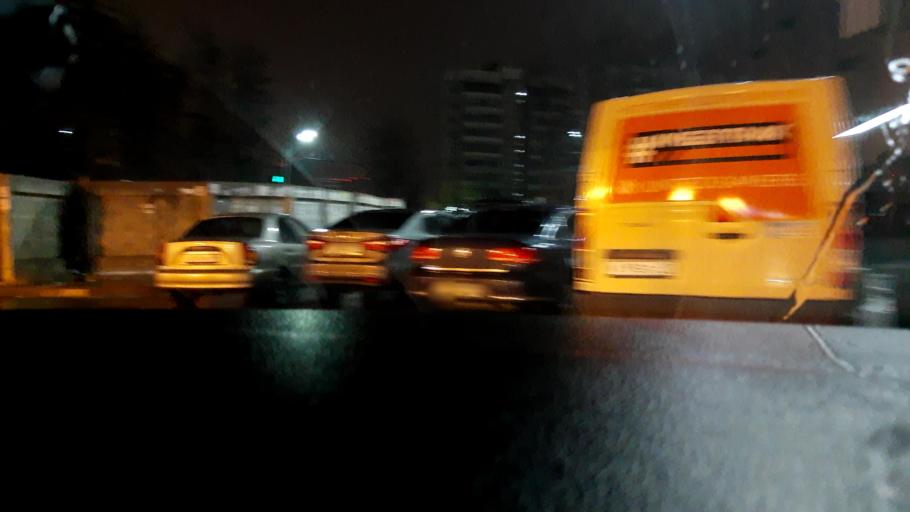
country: RU
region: Moskovskaya
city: Opalikha
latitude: 55.8349
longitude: 37.2810
